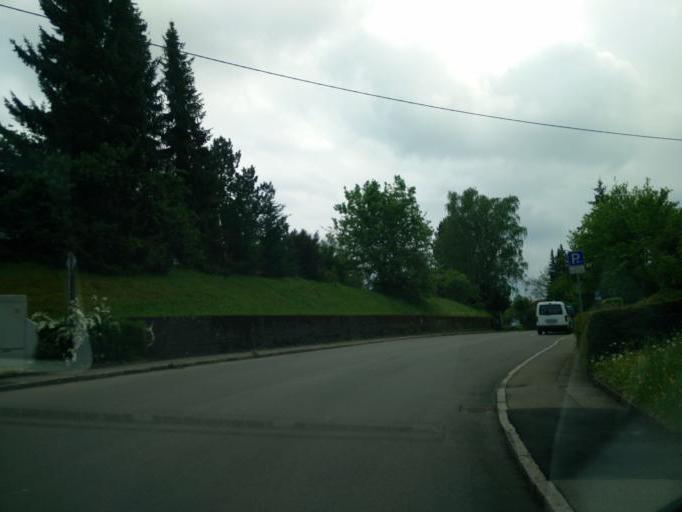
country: DE
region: Baden-Wuerttemberg
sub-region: Tuebingen Region
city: Gomaringen
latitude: 48.4833
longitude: 9.1133
